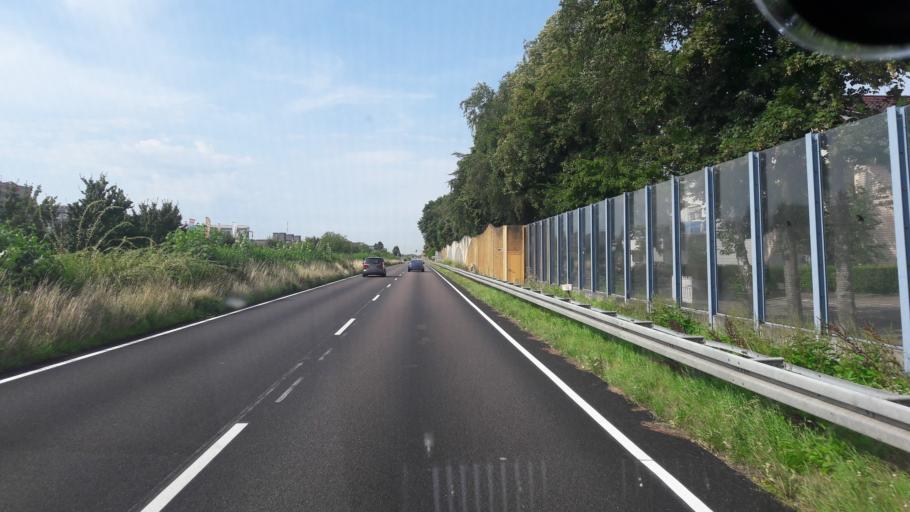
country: DE
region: Baden-Wuerttemberg
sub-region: Karlsruhe Region
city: Rheinstetten
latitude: 48.9655
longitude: 8.3068
